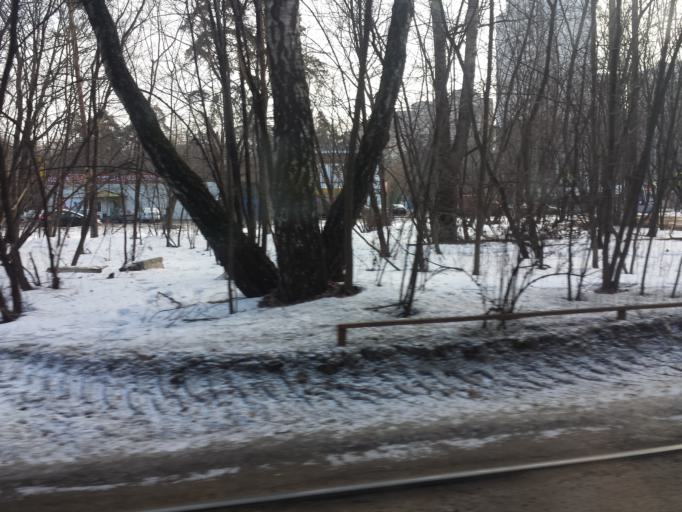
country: RU
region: Moscow
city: Pokrovskoye-Streshnevo
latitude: 55.8109
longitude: 37.4751
